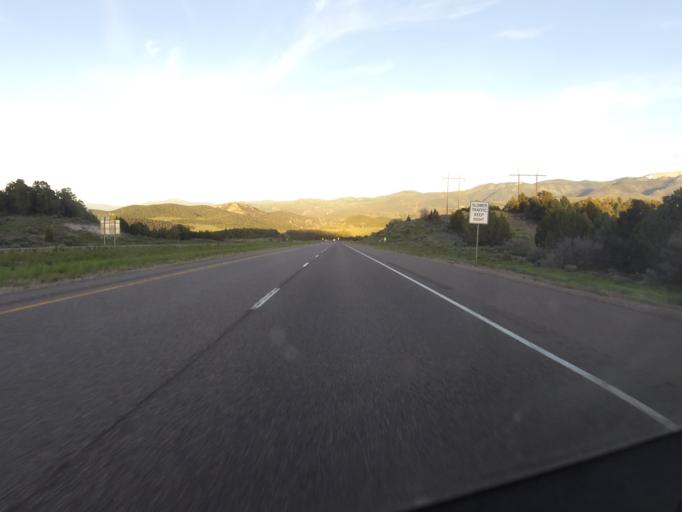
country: US
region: Utah
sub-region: Beaver County
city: Beaver
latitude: 38.5772
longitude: -112.4746
